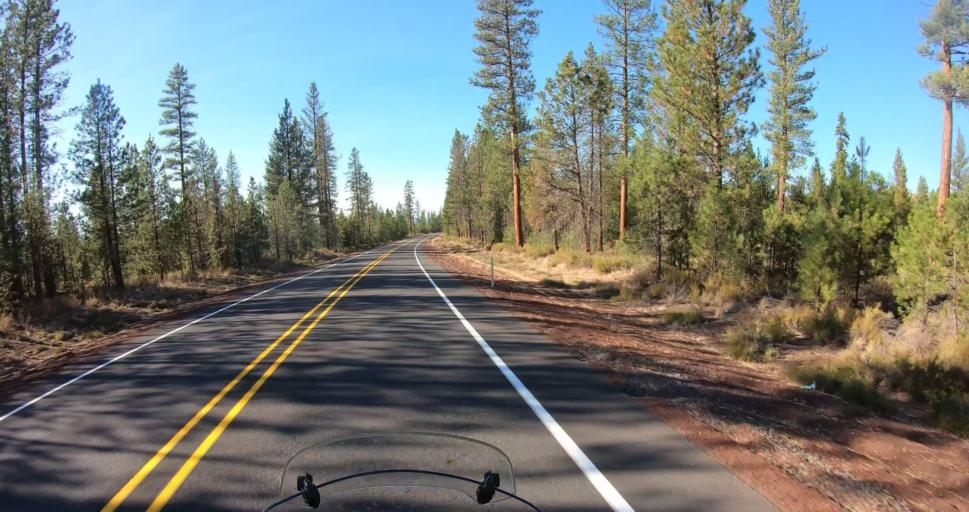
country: US
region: Oregon
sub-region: Deschutes County
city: La Pine
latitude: 43.4936
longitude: -121.4437
